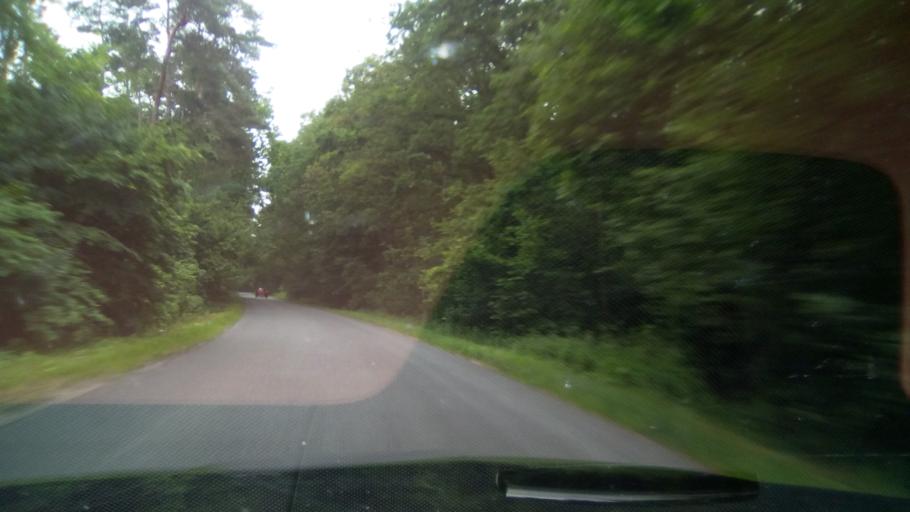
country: PL
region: Greater Poland Voivodeship
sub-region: Powiat gnieznienski
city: Czerniejewo
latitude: 52.4705
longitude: 17.5063
